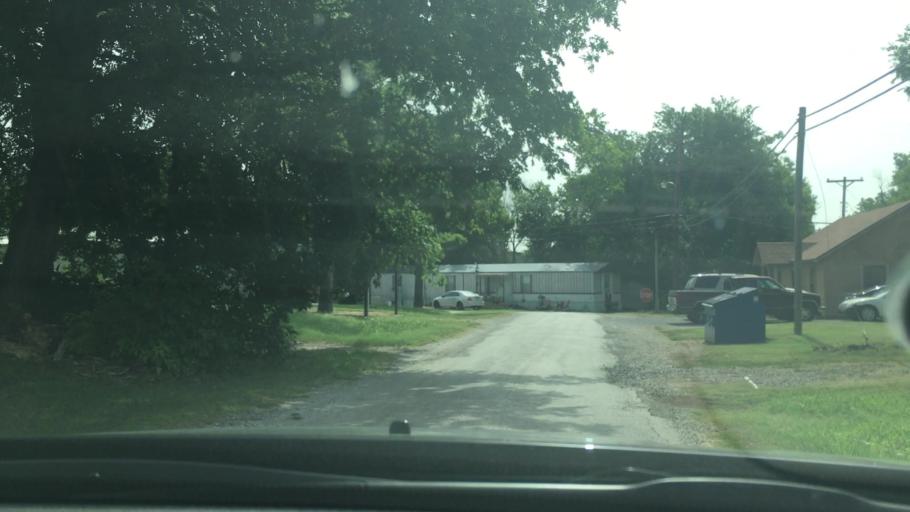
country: US
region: Oklahoma
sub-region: Garvin County
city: Pauls Valley
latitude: 34.8279
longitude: -97.2586
